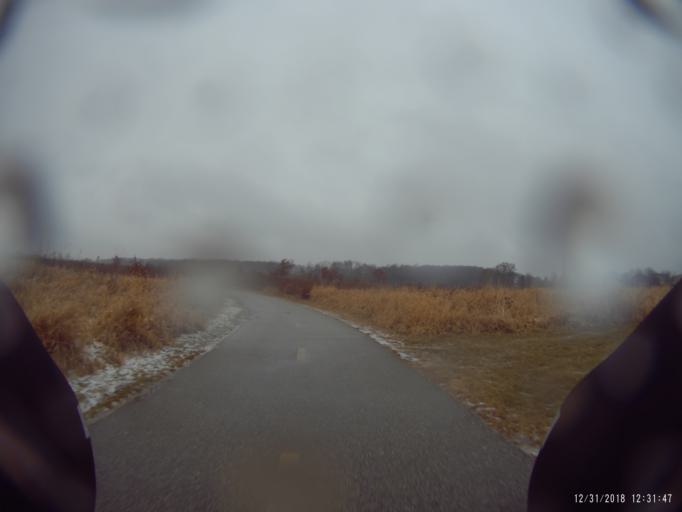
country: US
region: Wisconsin
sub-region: Dane County
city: Verona
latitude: 43.0065
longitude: -89.5164
